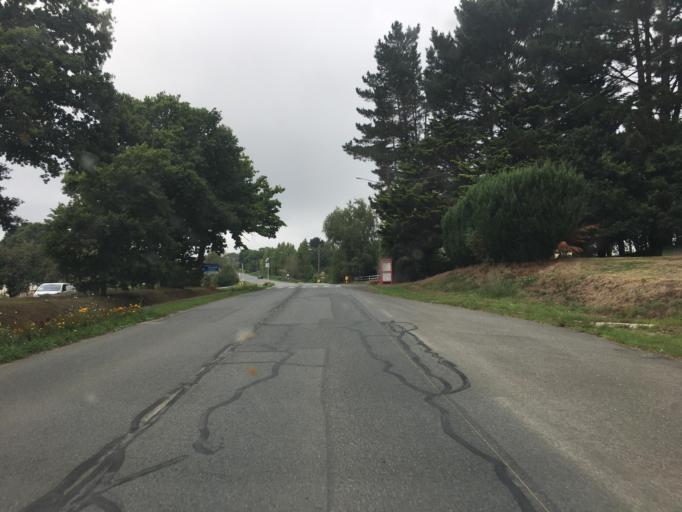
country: FR
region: Brittany
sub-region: Departement des Cotes-d'Armor
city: Gouarec
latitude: 48.2282
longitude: -3.1870
